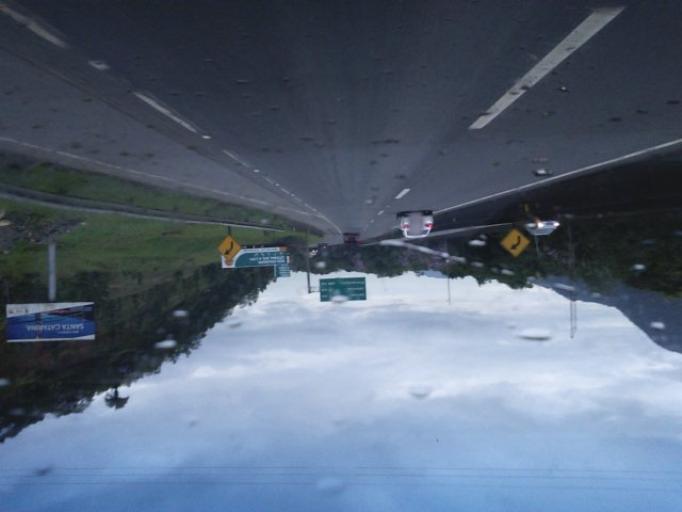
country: BR
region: Parana
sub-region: Guaratuba
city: Guaratuba
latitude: -25.9721
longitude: -48.8914
